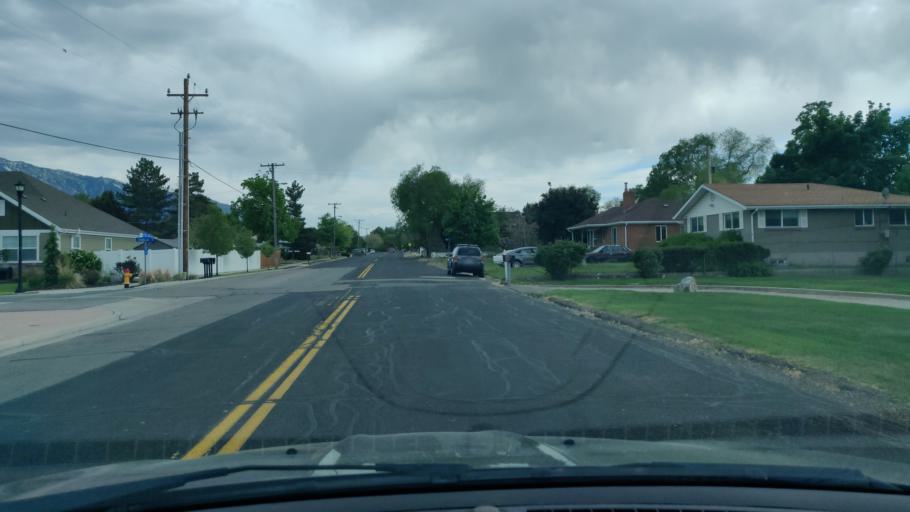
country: US
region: Utah
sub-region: Salt Lake County
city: Little Cottonwood Creek Valley
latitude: 40.6234
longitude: -111.8438
